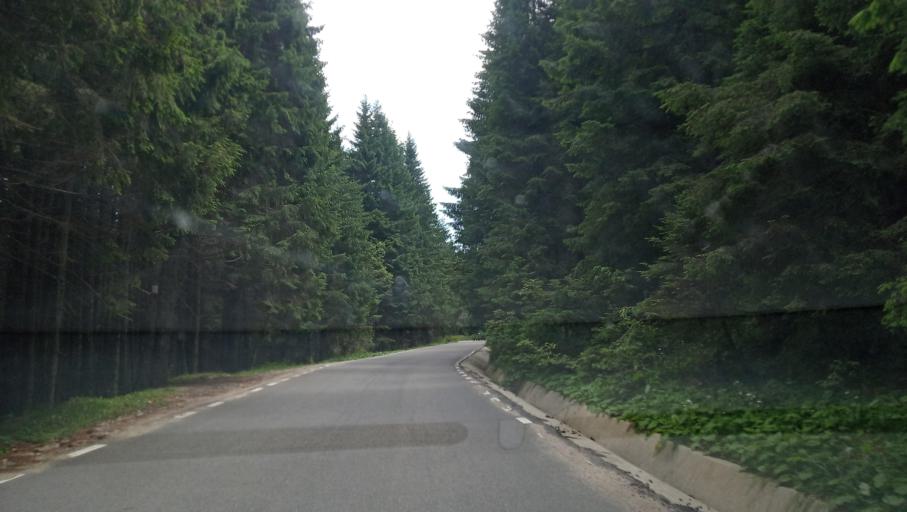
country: RO
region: Dambovita
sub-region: Comuna Moroeni
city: Glod
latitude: 45.3278
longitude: 25.4440
